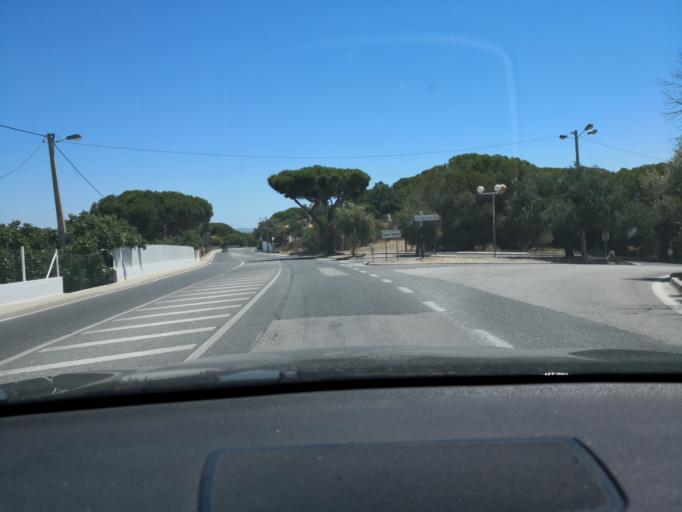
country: PT
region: Faro
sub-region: Albufeira
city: Ferreiras
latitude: 37.1084
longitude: -8.2054
